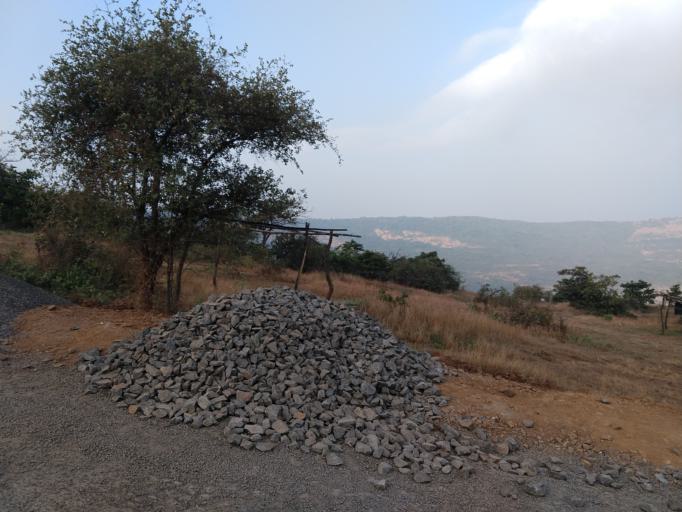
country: IN
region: Maharashtra
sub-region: Pune Division
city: Lonavla
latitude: 18.7217
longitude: 73.4780
